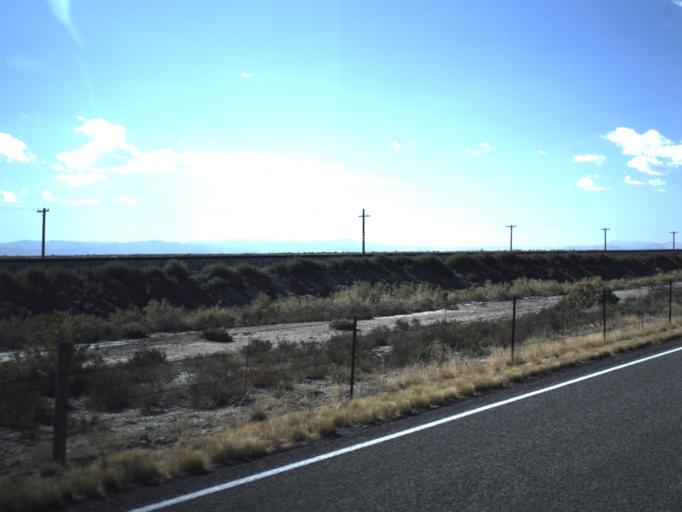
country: US
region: Utah
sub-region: Millard County
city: Delta
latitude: 39.1958
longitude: -112.6907
